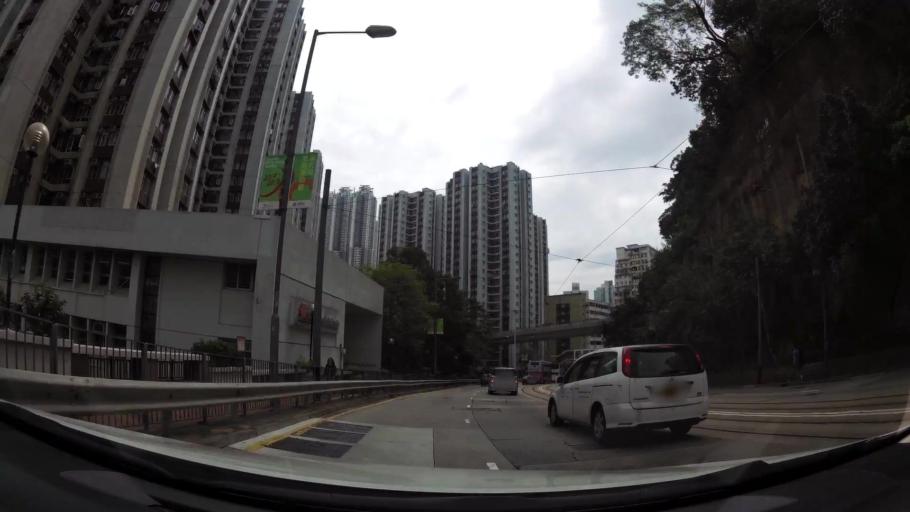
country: HK
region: Wanchai
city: Wan Chai
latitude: 22.2850
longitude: 114.2192
